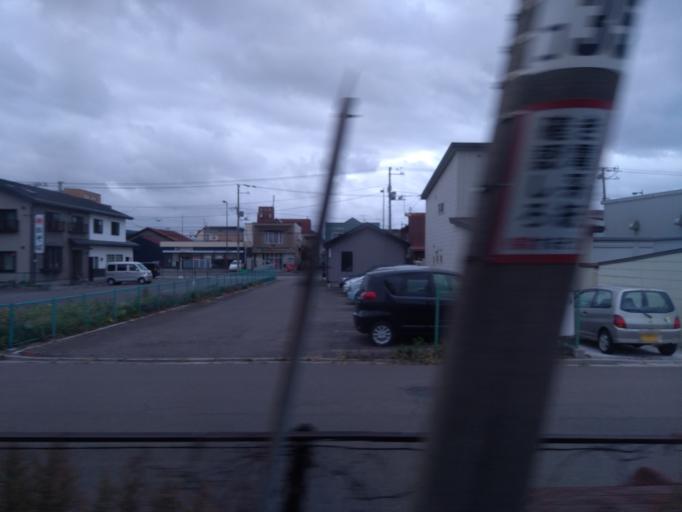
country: JP
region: Hokkaido
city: Hakodate
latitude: 41.7817
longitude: 140.7293
